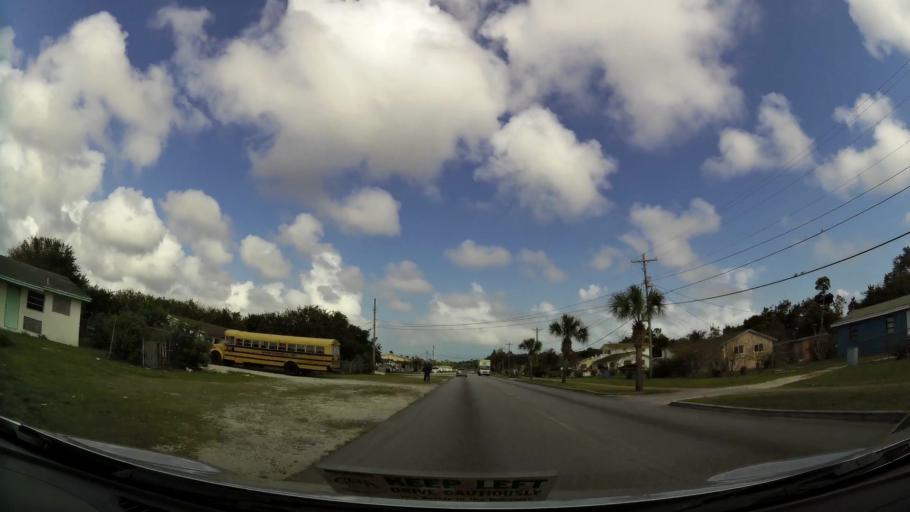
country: BS
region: Freeport
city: Freeport
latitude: 26.5294
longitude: -78.6847
